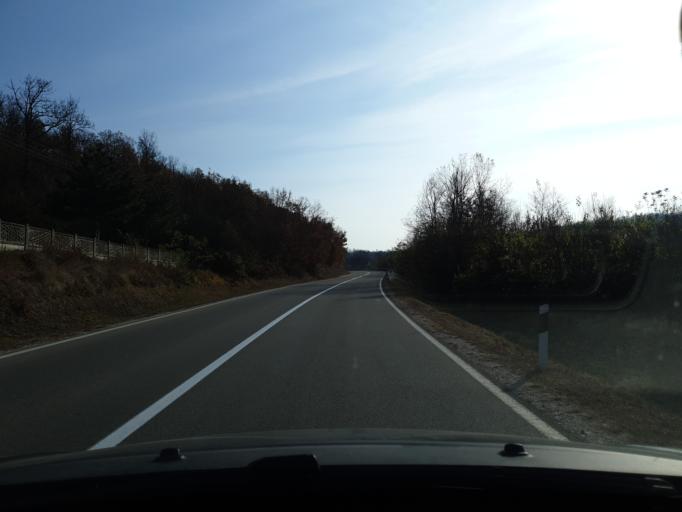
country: RS
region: Central Serbia
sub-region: Zajecarski Okrug
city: Zajecar
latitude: 43.9147
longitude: 22.1792
